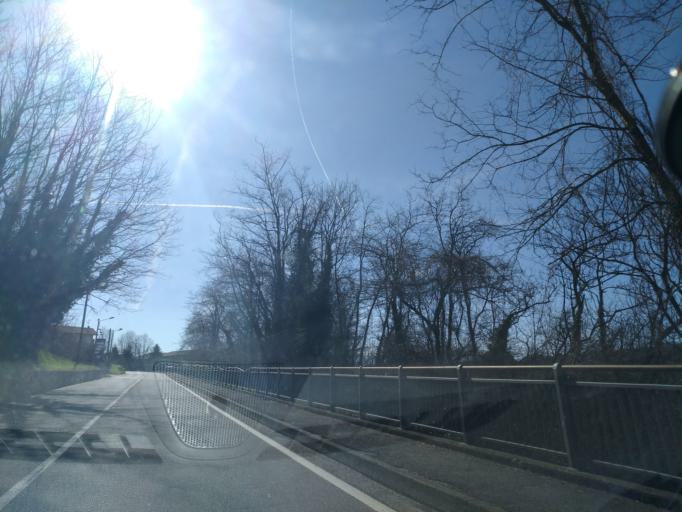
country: IT
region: Lombardy
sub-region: Provincia di Como
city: Lipomo
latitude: 45.7902
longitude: 9.1277
